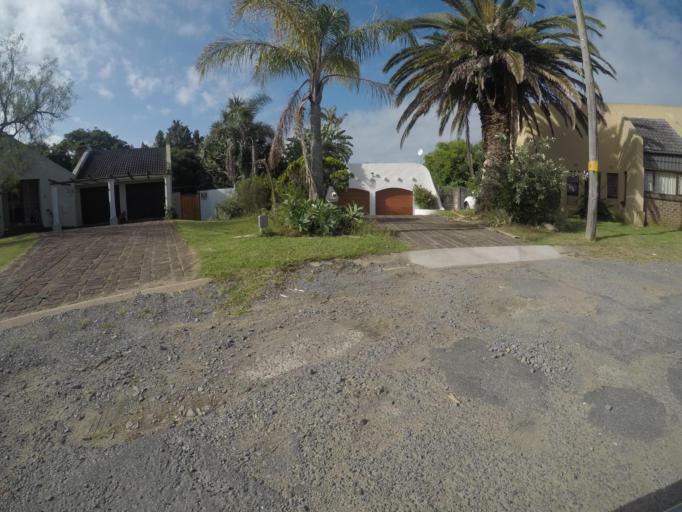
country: ZA
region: Eastern Cape
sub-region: Buffalo City Metropolitan Municipality
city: East London
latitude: -32.9719
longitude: 27.9559
